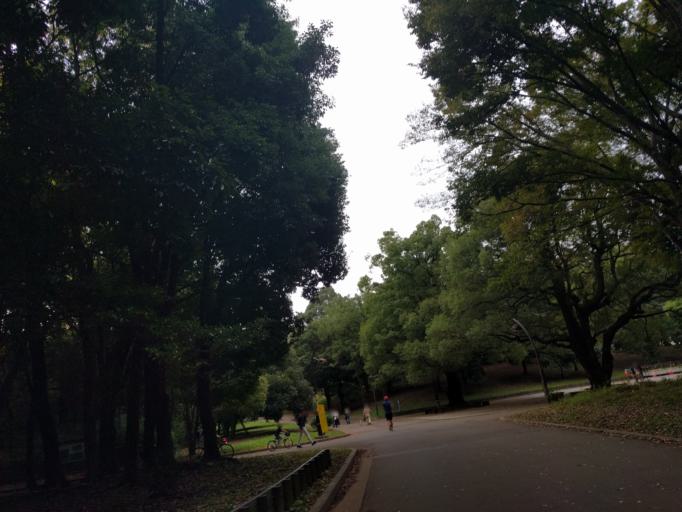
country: JP
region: Saitama
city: Wako
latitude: 35.7652
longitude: 139.6259
